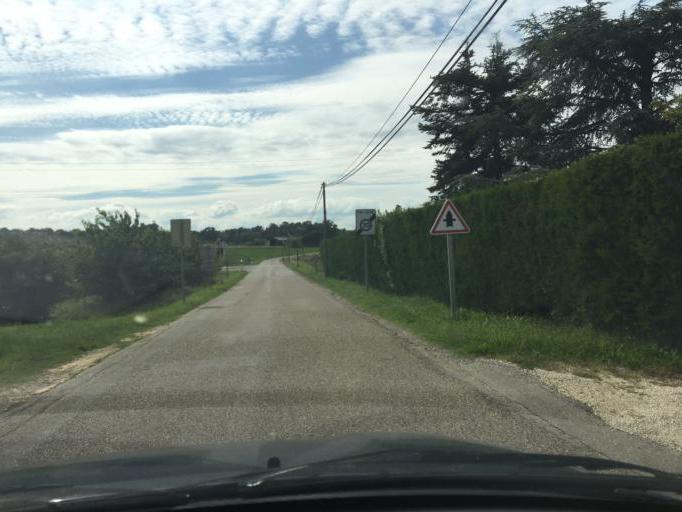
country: FR
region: Rhone-Alpes
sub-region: Departement de la Drome
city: Clerieux
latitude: 45.1180
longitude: 4.9413
